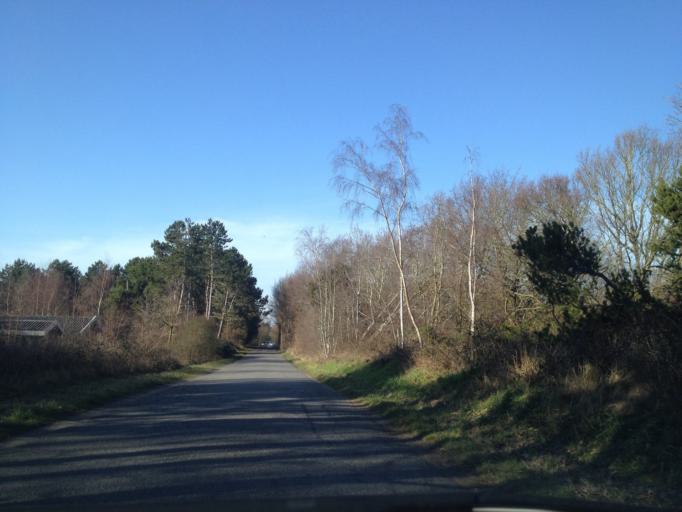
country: DK
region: South Denmark
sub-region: Kerteminde Kommune
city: Kerteminde
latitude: 55.5522
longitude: 10.6199
